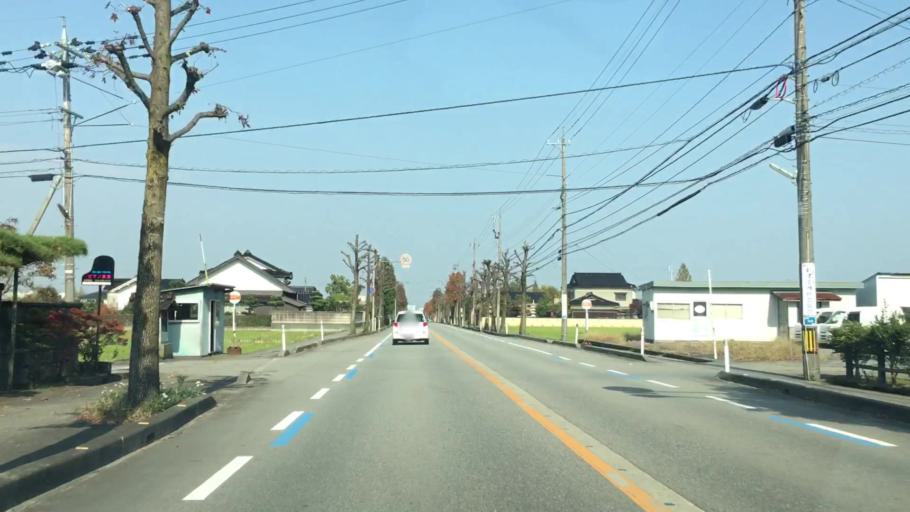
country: JP
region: Toyama
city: Toyama-shi
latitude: 36.6372
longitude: 137.1938
